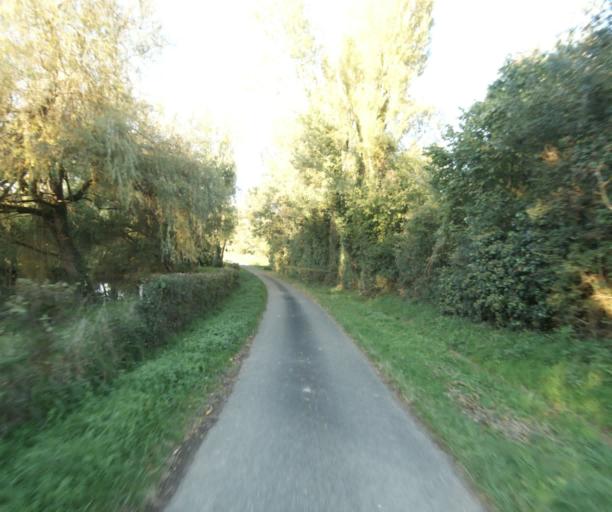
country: FR
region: Midi-Pyrenees
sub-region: Departement du Gers
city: Eauze
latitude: 43.7393
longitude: 0.1666
